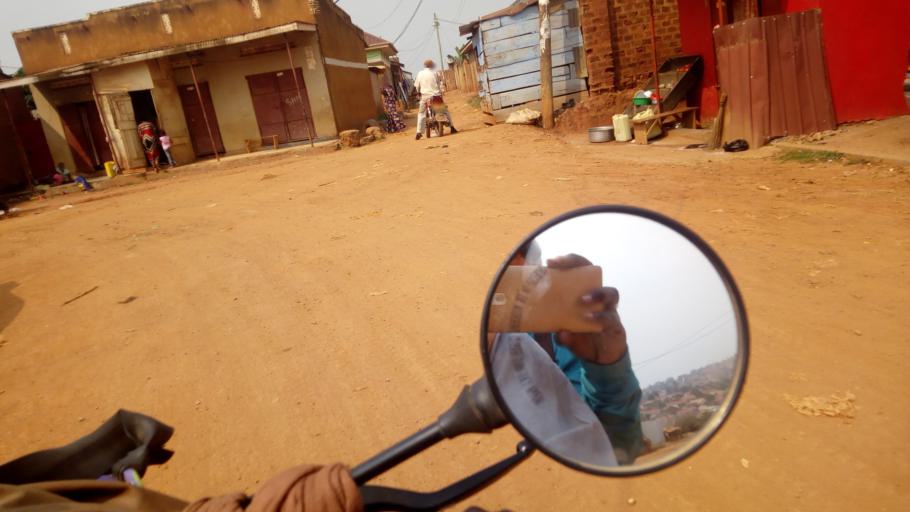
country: UG
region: Central Region
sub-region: Wakiso District
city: Kireka
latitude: 0.3232
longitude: 32.6538
